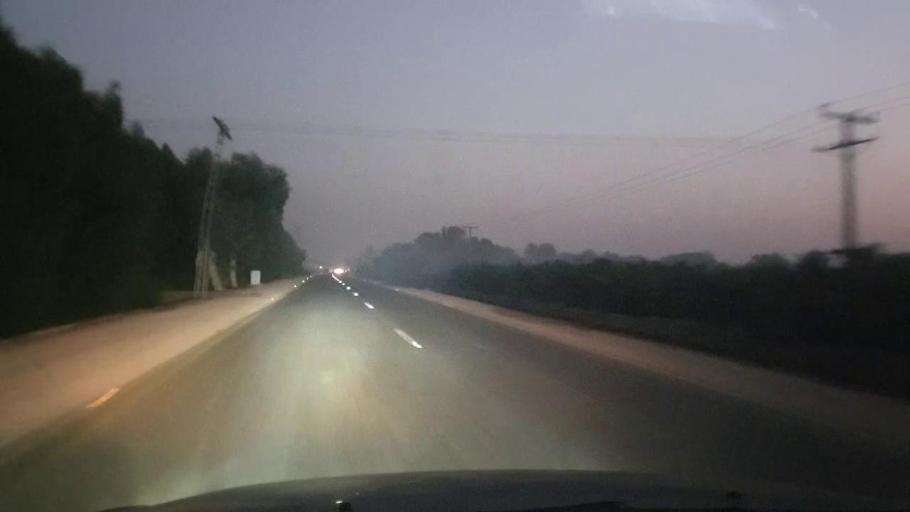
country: PK
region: Sindh
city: Chambar
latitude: 25.3676
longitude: 68.7831
